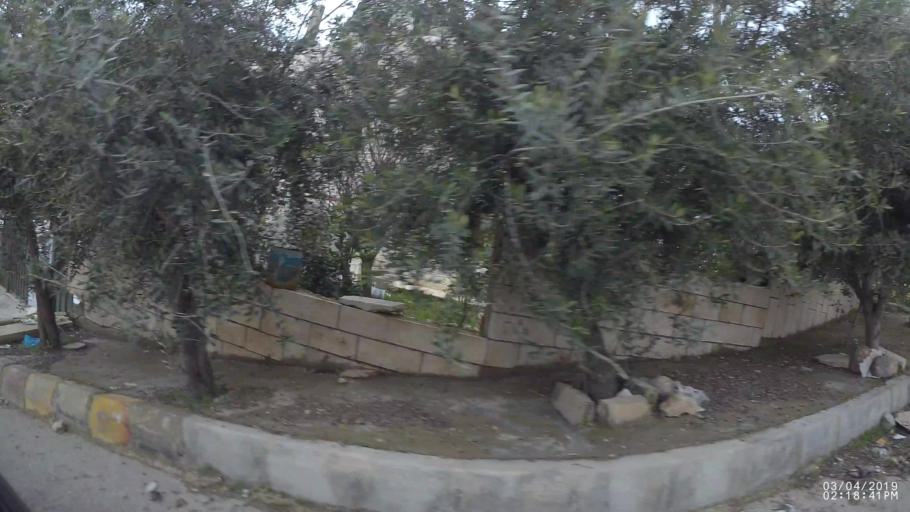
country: JO
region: Amman
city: Wadi as Sir
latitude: 31.9397
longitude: 35.8324
